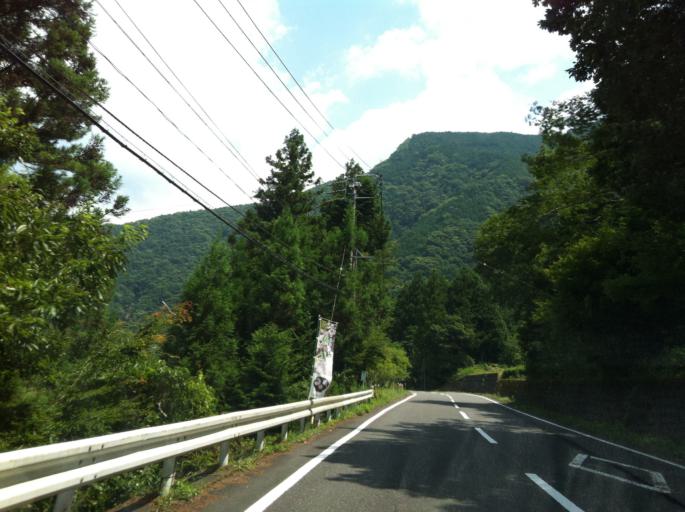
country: JP
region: Shizuoka
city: Shizuoka-shi
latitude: 35.2613
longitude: 138.3280
